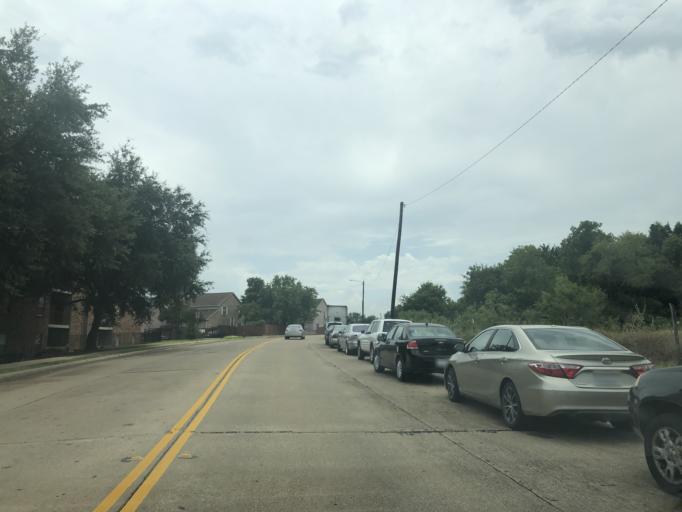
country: US
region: Texas
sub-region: Dallas County
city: Grand Prairie
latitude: 32.7530
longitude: -97.0368
